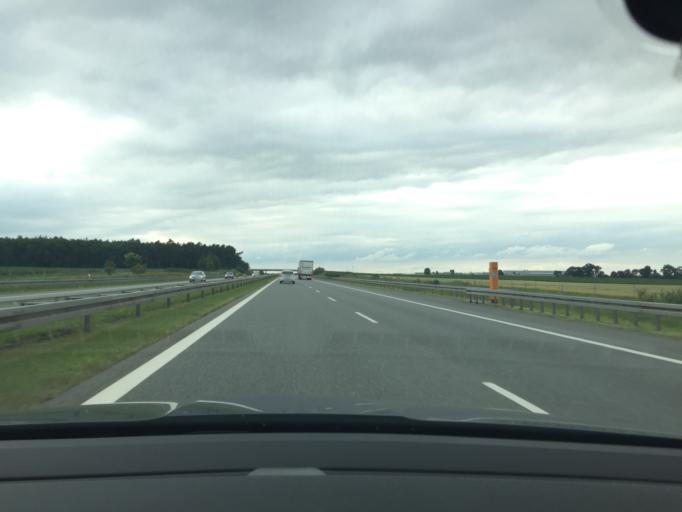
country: PL
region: Greater Poland Voivodeship
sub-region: Powiat poznanski
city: Dopiewo
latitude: 52.3618
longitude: 16.6069
